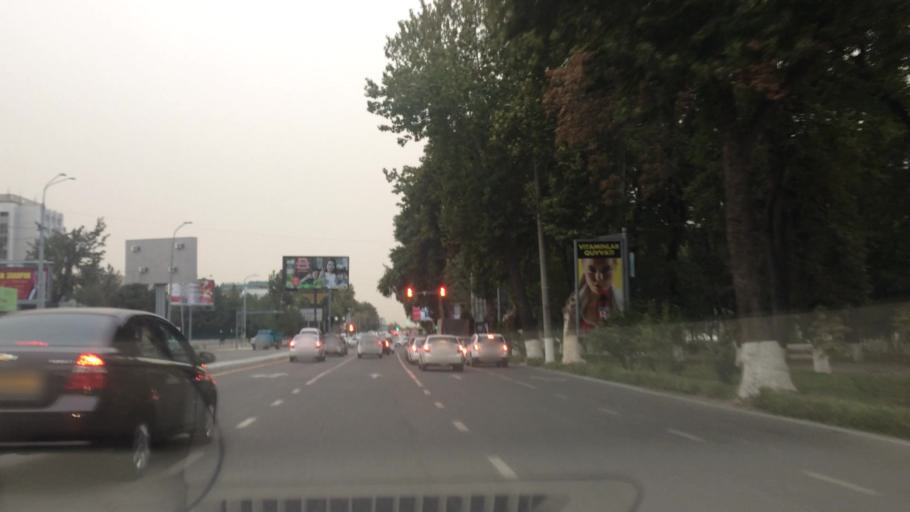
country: UZ
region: Toshkent Shahri
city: Tashkent
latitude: 41.3038
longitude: 69.2803
